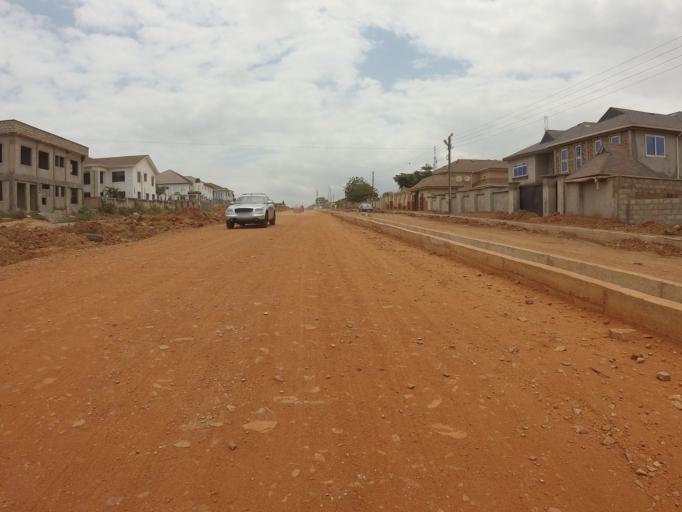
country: GH
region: Greater Accra
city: Medina Estates
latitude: 5.6296
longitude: -0.1418
